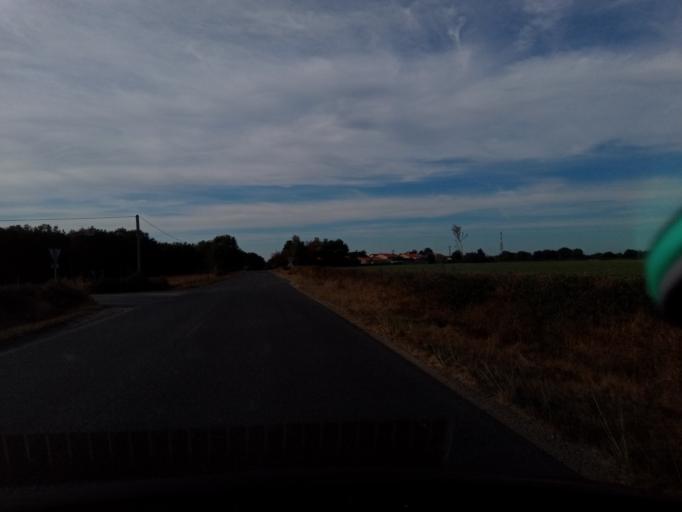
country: FR
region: Poitou-Charentes
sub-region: Departement de la Vienne
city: Montmorillon
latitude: 46.4107
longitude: 0.8870
